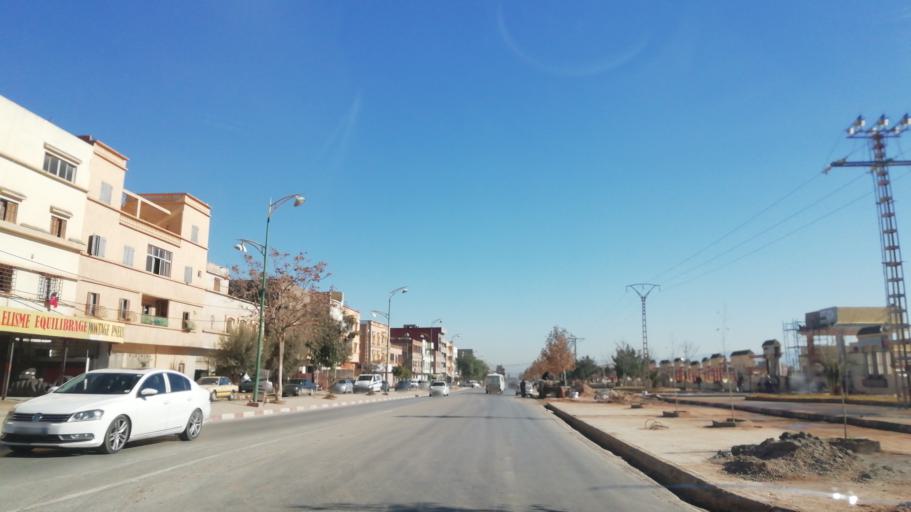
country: DZ
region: Tlemcen
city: Nedroma
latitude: 34.8444
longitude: -1.7560
